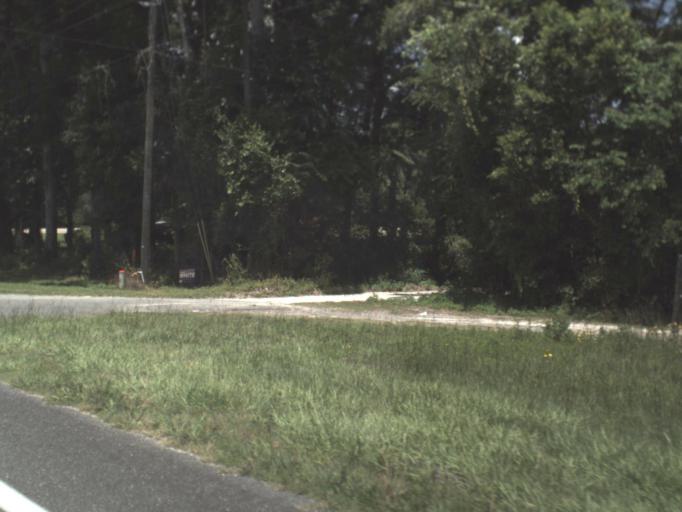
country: US
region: Florida
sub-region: Suwannee County
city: Wellborn
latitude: 29.9524
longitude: -82.8686
